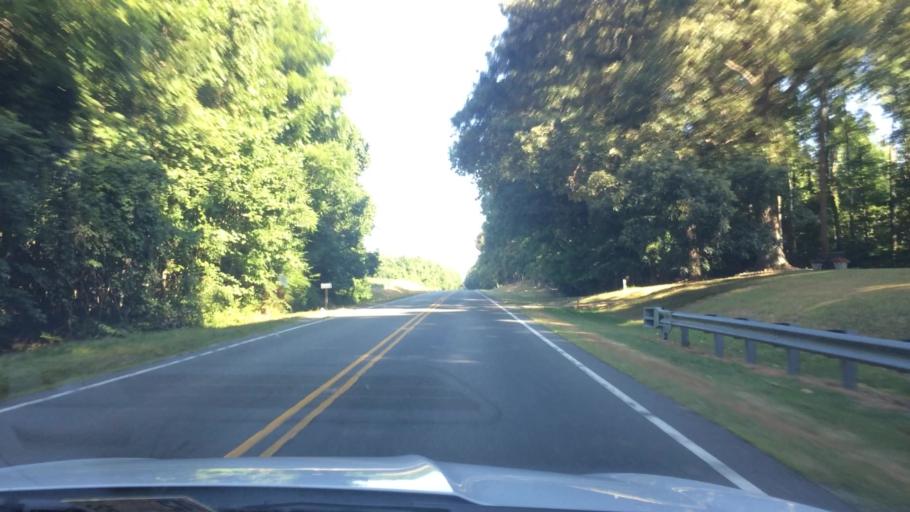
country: US
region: Virginia
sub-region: Lancaster County
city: Lancaster
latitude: 37.8013
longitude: -76.5313
